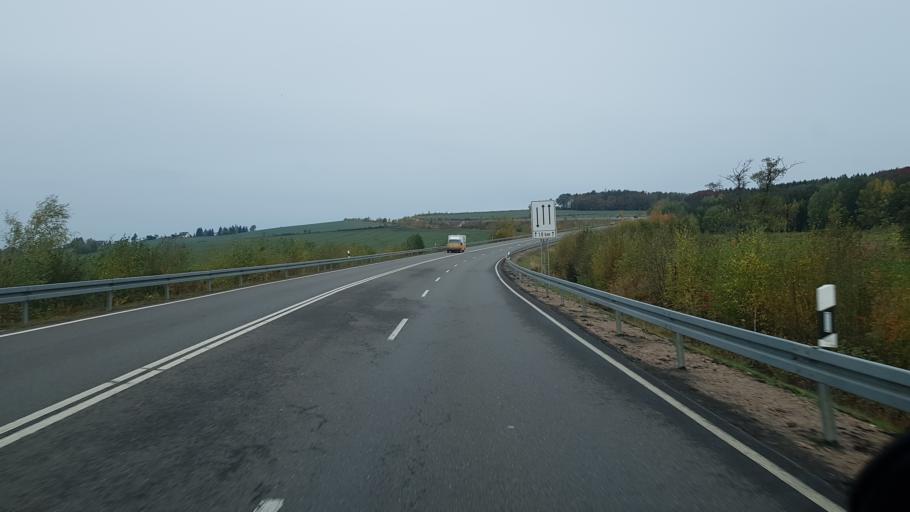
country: DE
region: Saxony
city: Hirschfeld
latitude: 50.6321
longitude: 12.4579
